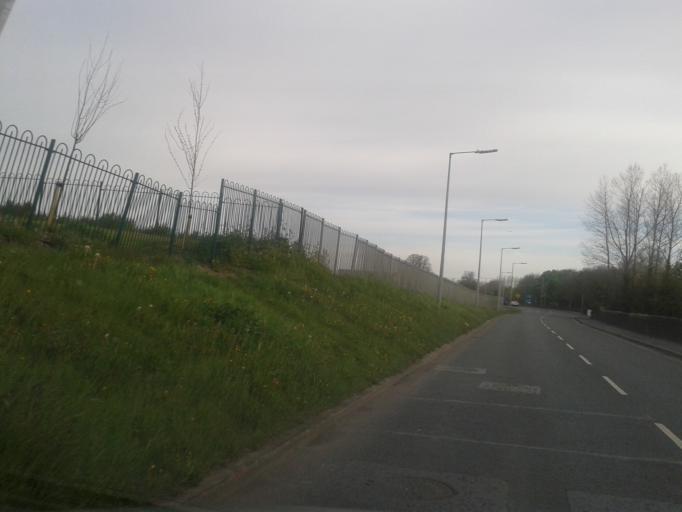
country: IE
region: Leinster
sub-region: Fingal County
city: Swords
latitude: 53.4662
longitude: -6.2193
